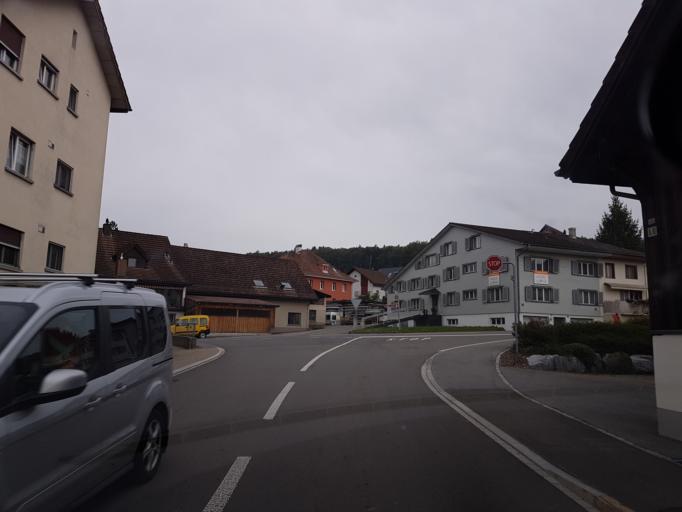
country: CH
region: Saint Gallen
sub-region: Wahlkreis See-Gaster
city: Schmerikon
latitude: 47.2488
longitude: 8.9447
